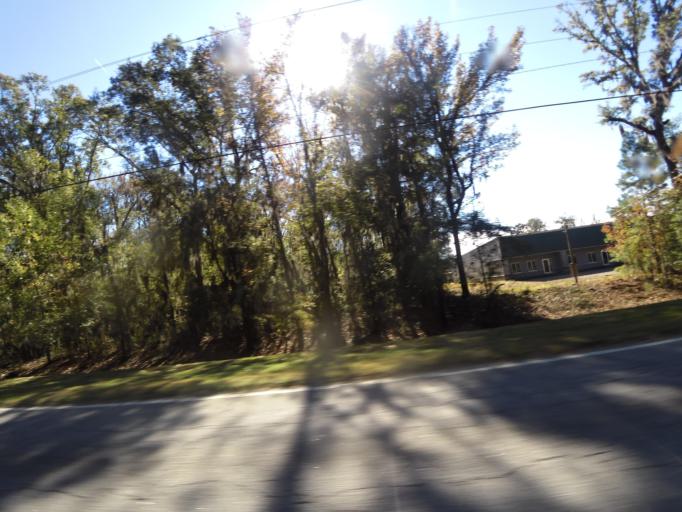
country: US
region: Georgia
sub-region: Chatham County
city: Savannah
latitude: 32.0770
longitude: -81.1271
